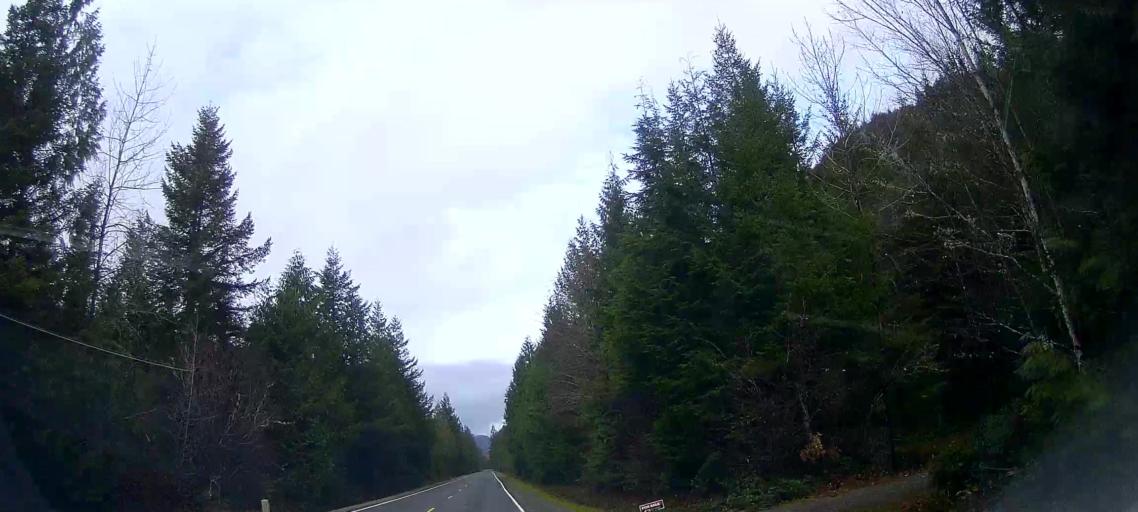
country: US
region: Washington
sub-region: Snohomish County
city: Darrington
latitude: 48.5083
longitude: -121.4571
